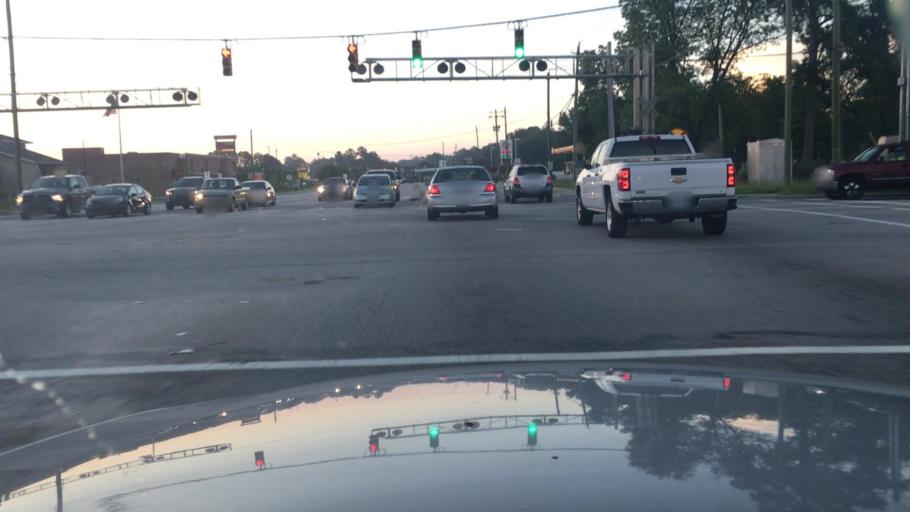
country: US
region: North Carolina
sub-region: Cumberland County
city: Fort Bragg
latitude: 35.0614
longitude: -79.0155
